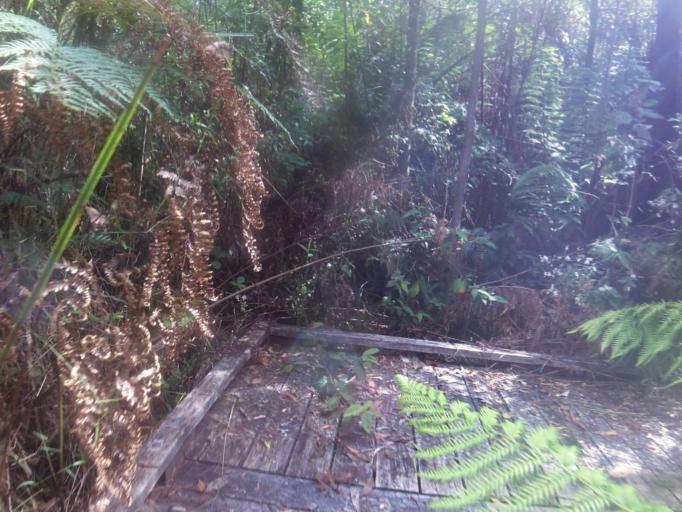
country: AU
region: Victoria
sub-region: Yarra Ranges
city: Millgrove
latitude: -37.5161
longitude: 145.7454
